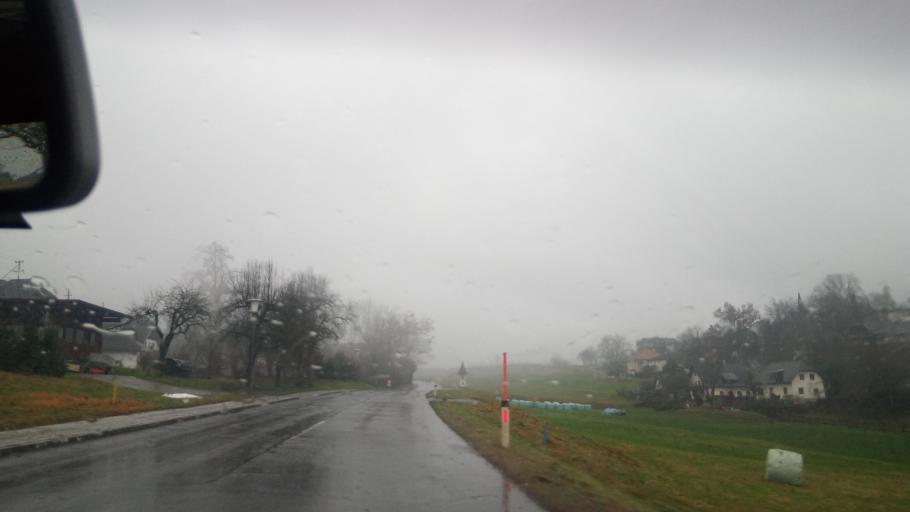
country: AT
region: Carinthia
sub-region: Politischer Bezirk Klagenfurt Land
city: Keutschach am See
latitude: 46.5891
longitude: 14.2152
